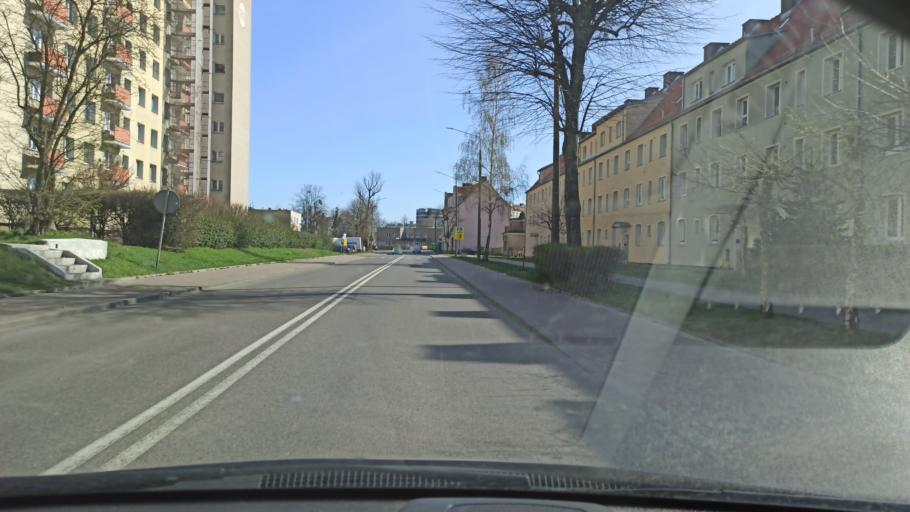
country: PL
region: Warmian-Masurian Voivodeship
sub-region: Powiat elblaski
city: Elblag
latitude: 54.1744
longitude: 19.4026
